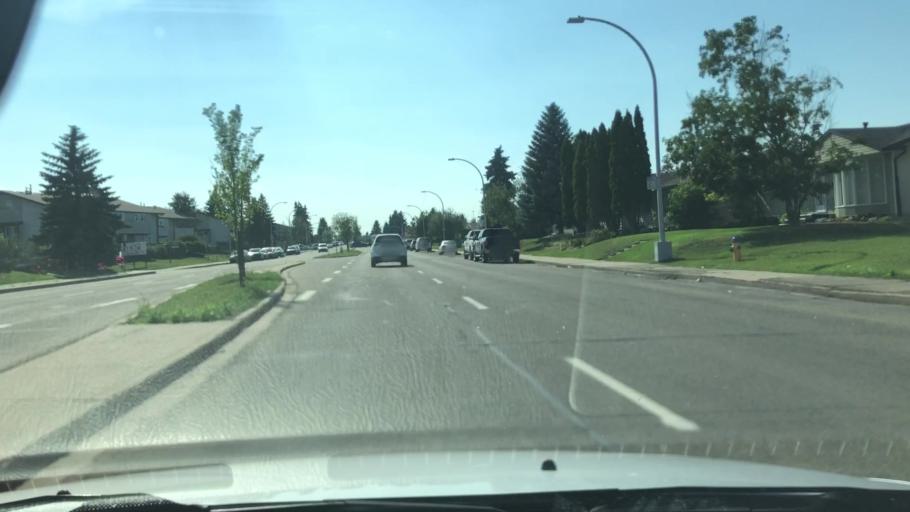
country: CA
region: Alberta
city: Edmonton
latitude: 53.6070
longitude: -113.4638
